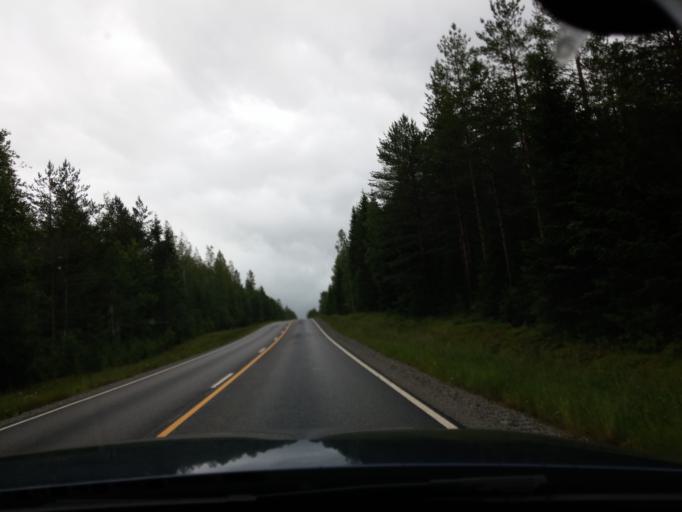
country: FI
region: Central Finland
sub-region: Saarijaervi-Viitasaari
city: Pylkoenmaeki
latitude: 62.6425
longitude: 24.8945
